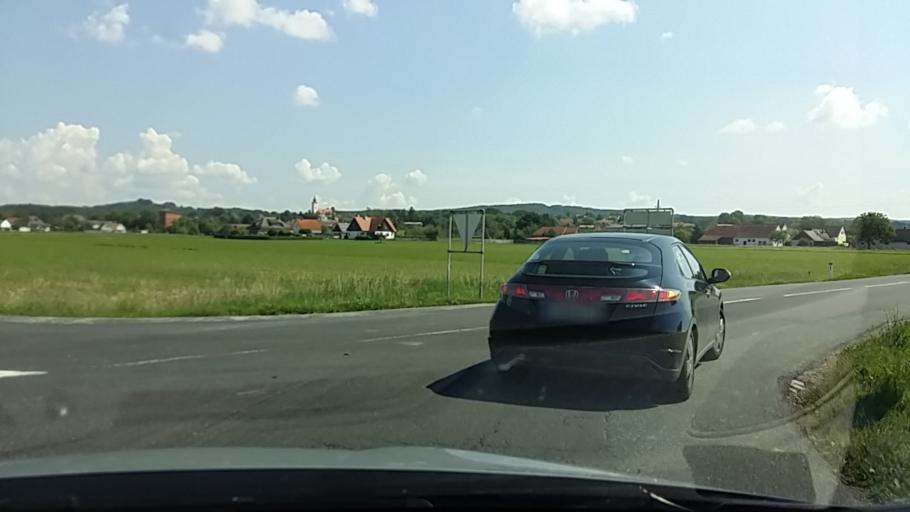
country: AT
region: Burgenland
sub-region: Politischer Bezirk Jennersdorf
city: Heiligenkreuz im Lafnitztal
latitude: 46.9827
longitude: 16.2541
